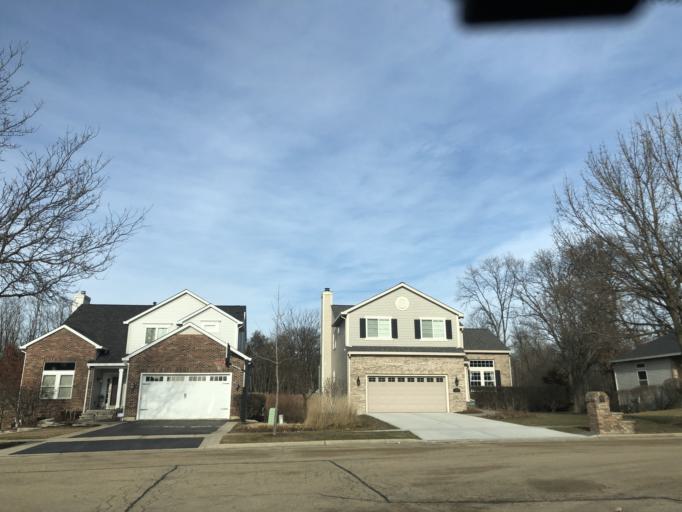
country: US
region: Illinois
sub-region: DuPage County
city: Woodridge
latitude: 41.7205
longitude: -88.0143
